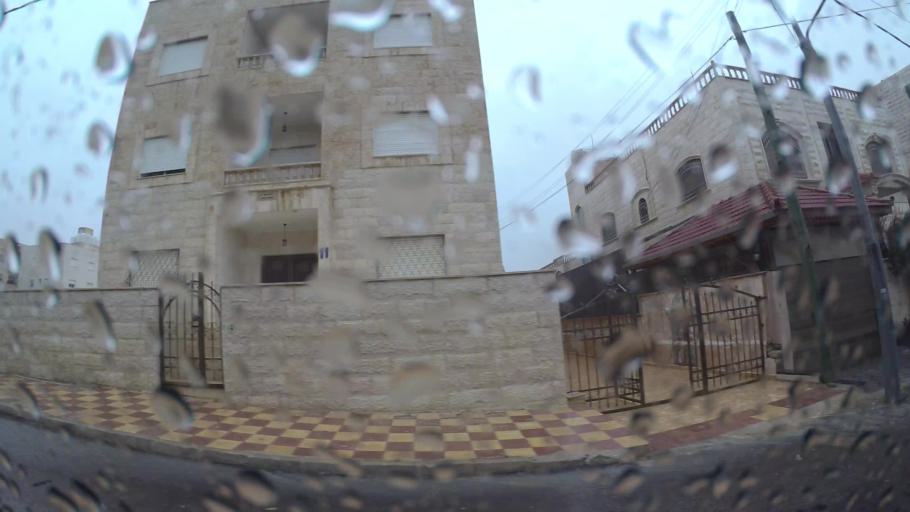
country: JO
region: Amman
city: Al Jubayhah
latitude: 32.0333
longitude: 35.8853
